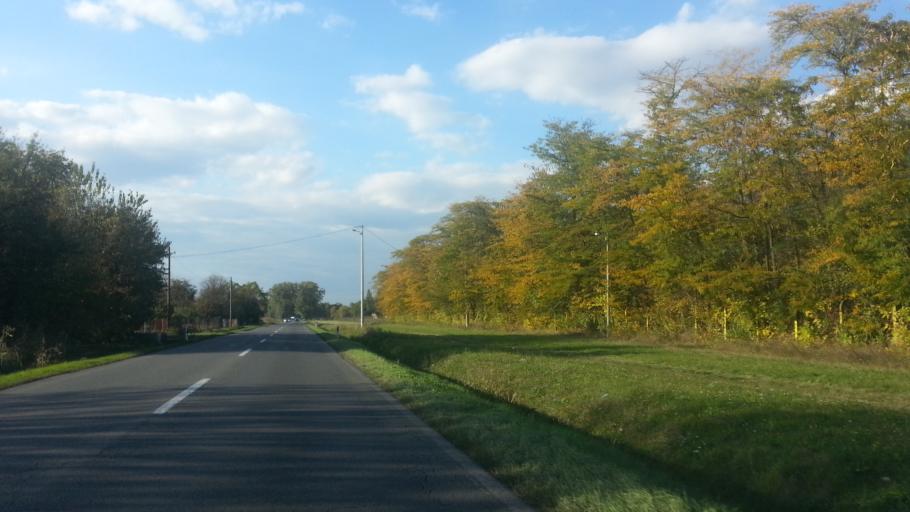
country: RS
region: Autonomna Pokrajina Vojvodina
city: Nova Pazova
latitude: 44.9195
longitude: 20.2520
